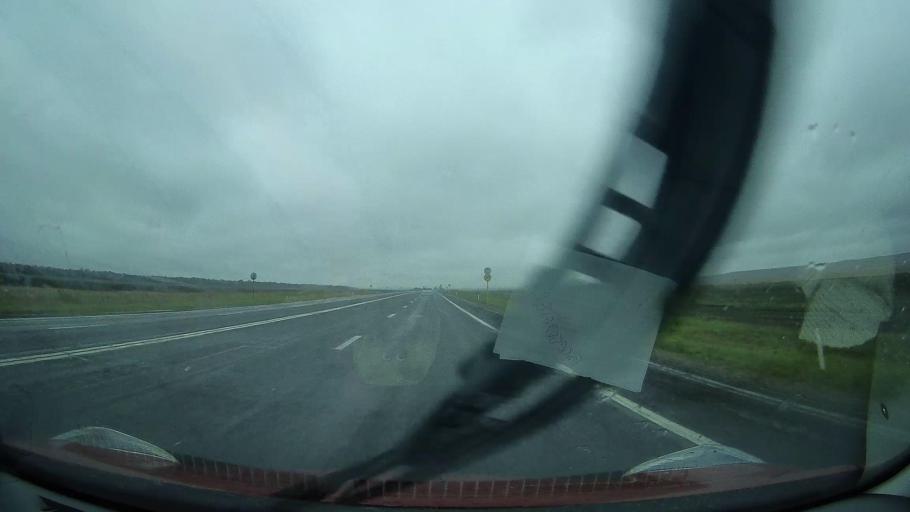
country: RU
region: Stavropol'skiy
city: Nevinnomyssk
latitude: 44.6266
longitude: 42.0522
